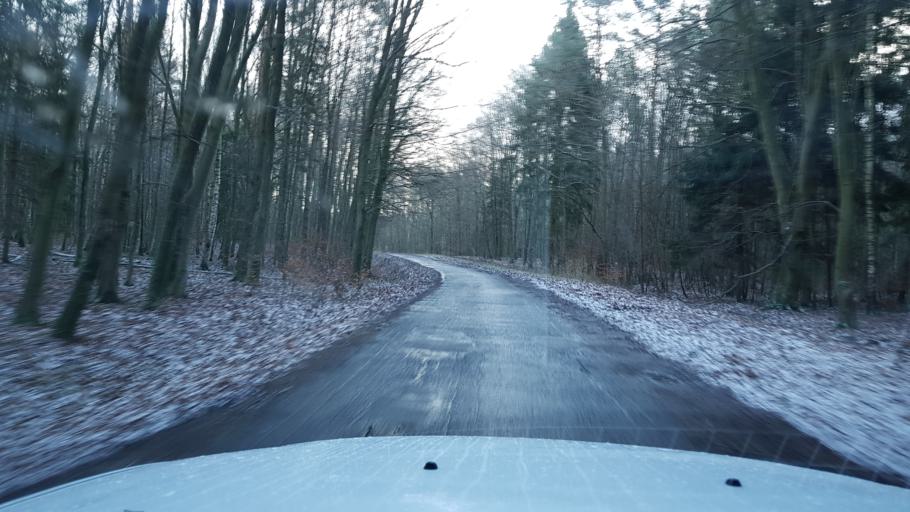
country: PL
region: West Pomeranian Voivodeship
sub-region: Powiat gryficki
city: Trzebiatow
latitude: 54.0433
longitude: 15.3313
